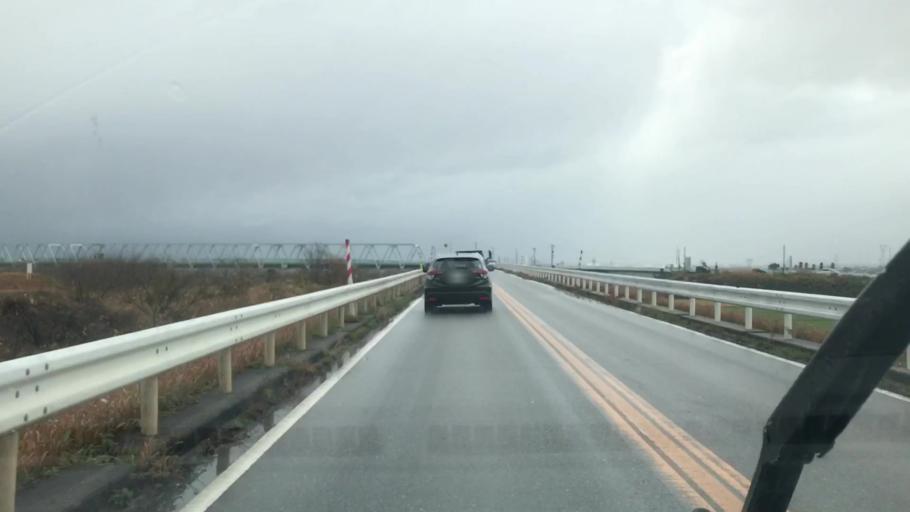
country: JP
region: Toyama
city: Toyama-shi
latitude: 36.6700
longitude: 137.2866
